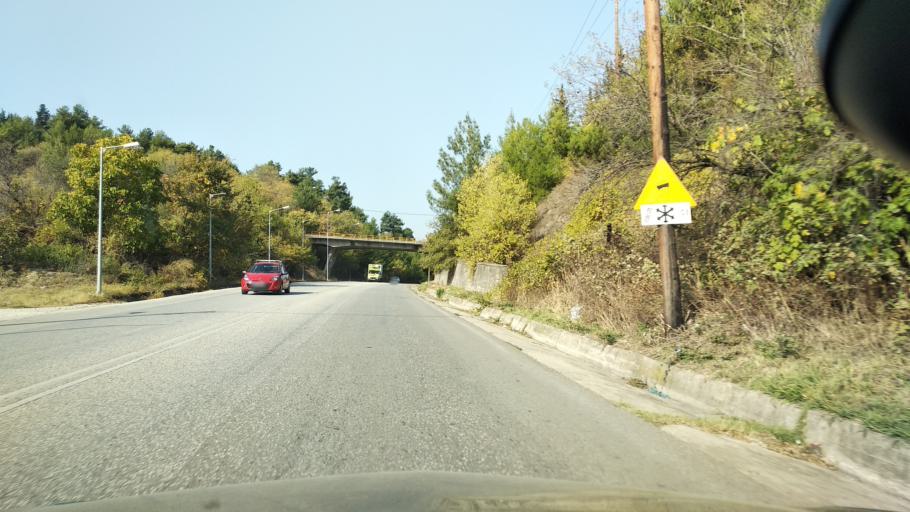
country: GR
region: Thessaly
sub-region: Trikala
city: Trikala
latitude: 39.5679
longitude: 21.7676
